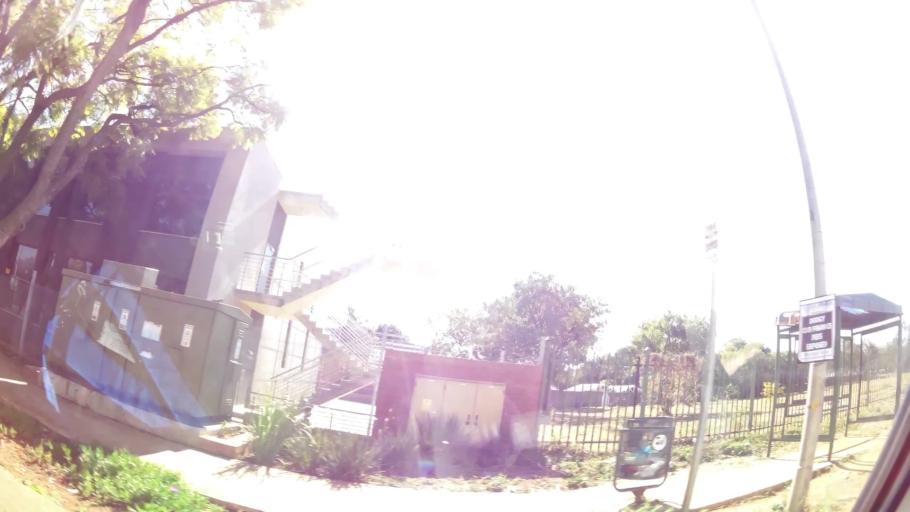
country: ZA
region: Gauteng
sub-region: City of Tshwane Metropolitan Municipality
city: Pretoria
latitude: -25.7627
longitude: 28.2604
